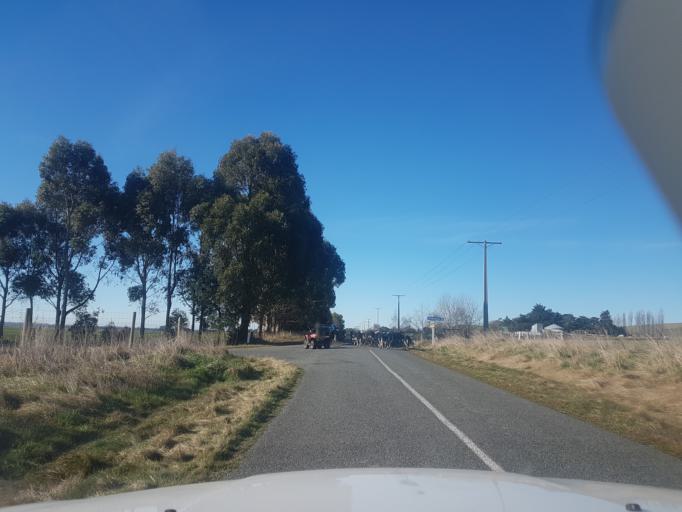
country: NZ
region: Canterbury
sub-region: Timaru District
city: Pleasant Point
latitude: -44.2908
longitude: 171.0635
